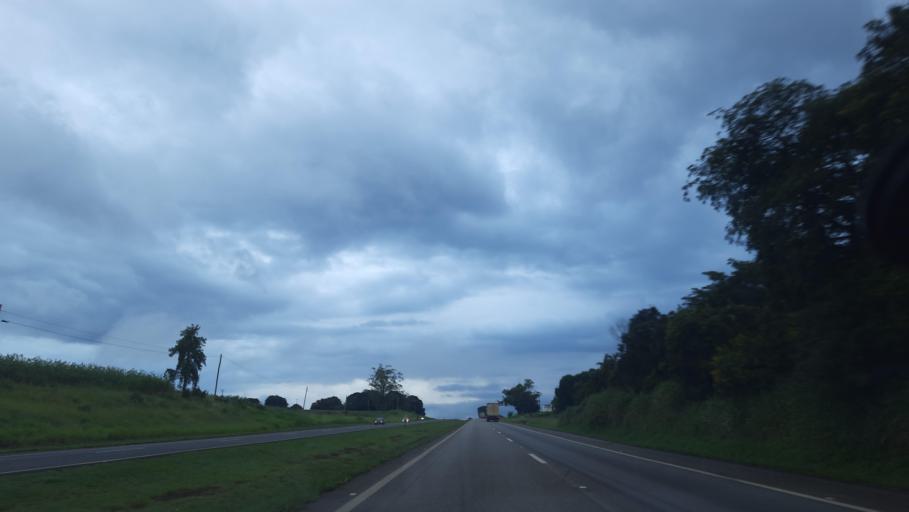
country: BR
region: Sao Paulo
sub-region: Moji-Guacu
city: Mogi-Gaucu
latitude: -22.2490
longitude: -46.9778
